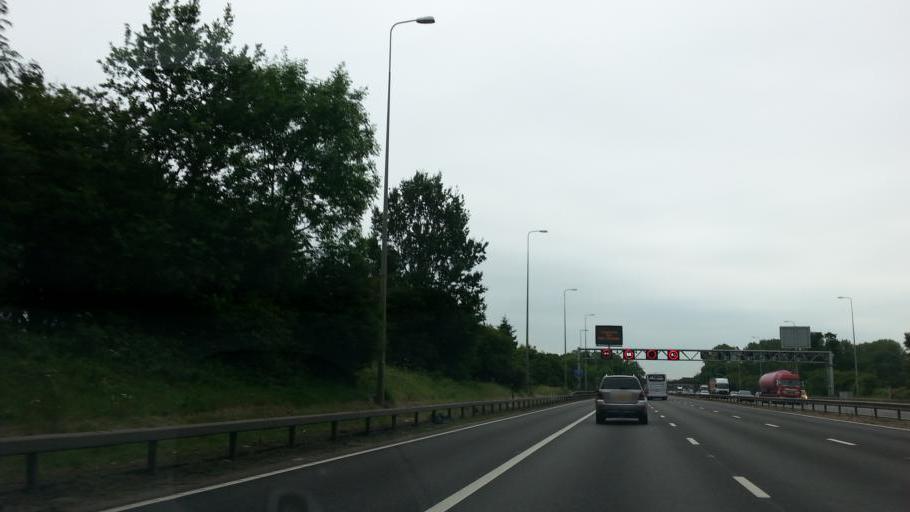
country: GB
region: England
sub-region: Solihull
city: Bickenhill
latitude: 52.4274
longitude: -1.7182
